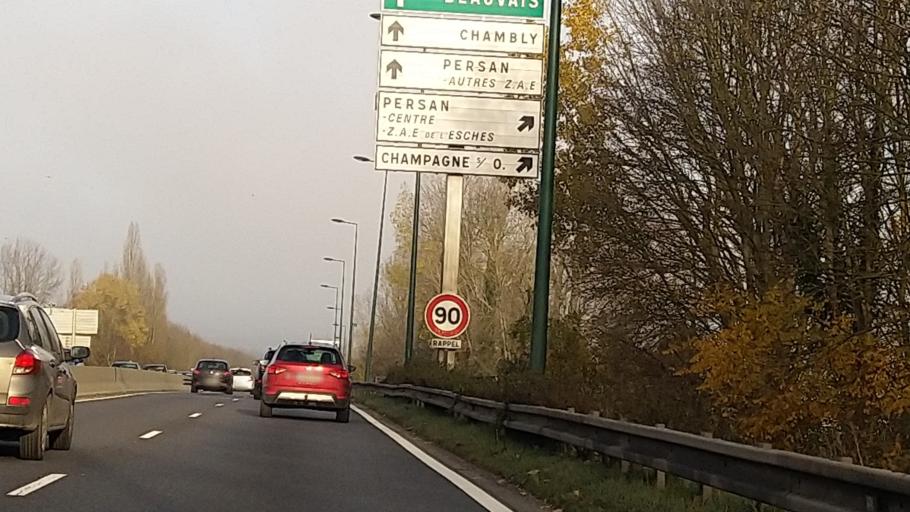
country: FR
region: Ile-de-France
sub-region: Departement du Val-d'Oise
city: Champagne-sur-Oise
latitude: 49.1380
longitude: 2.2536
